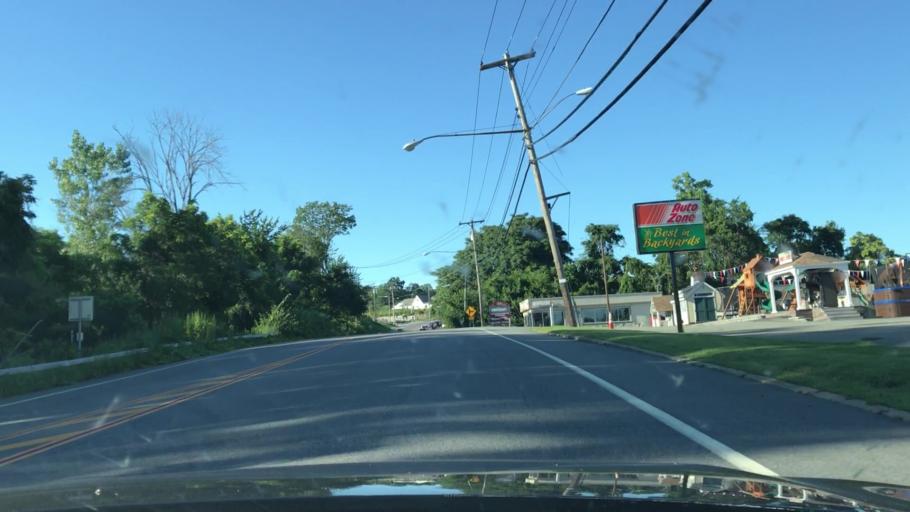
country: US
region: New York
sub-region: Westchester County
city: Shenorock
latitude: 41.3459
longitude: -73.7567
